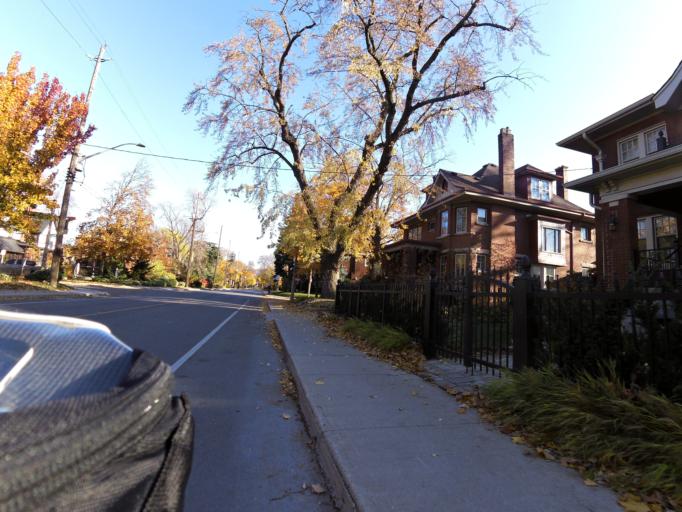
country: CA
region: Ontario
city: Hamilton
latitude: 43.2468
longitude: -79.8451
